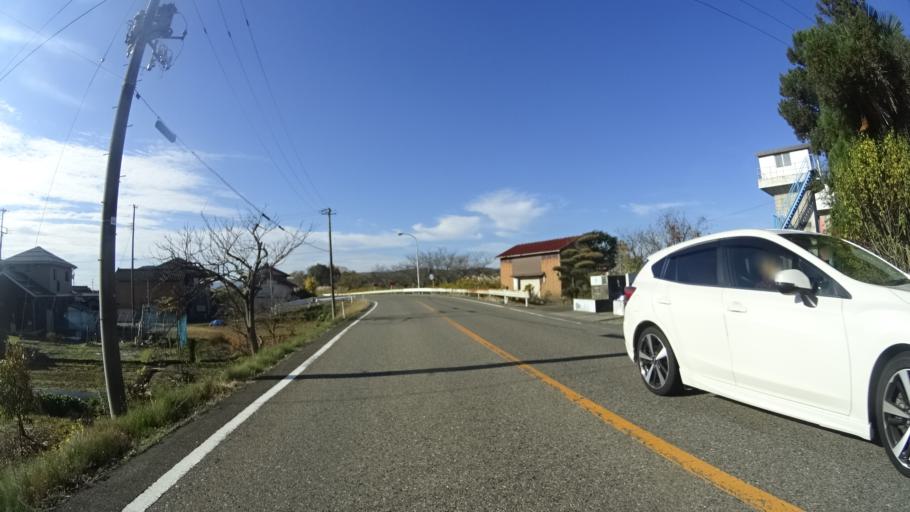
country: JP
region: Niigata
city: Yoshida-kasugacho
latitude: 37.5905
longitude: 138.8377
